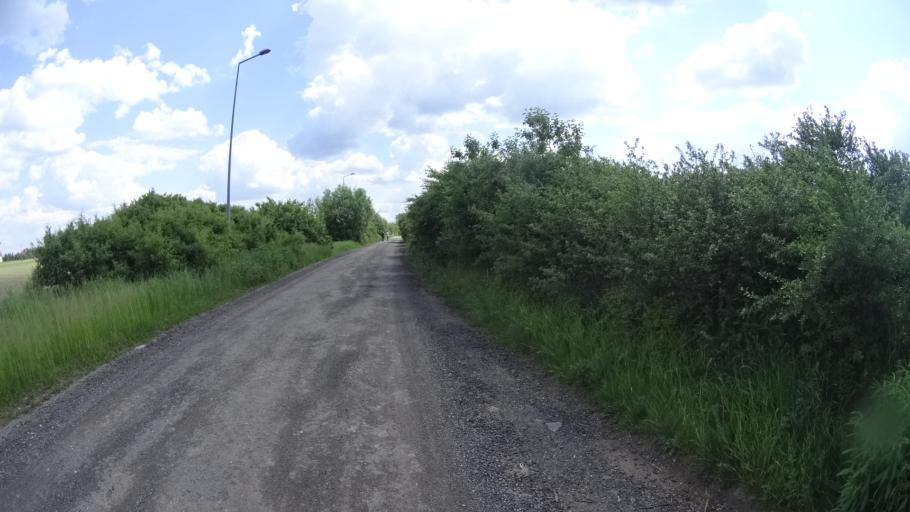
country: PL
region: Masovian Voivodeship
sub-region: Powiat pruszkowski
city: Nadarzyn
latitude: 52.0570
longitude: 20.8237
